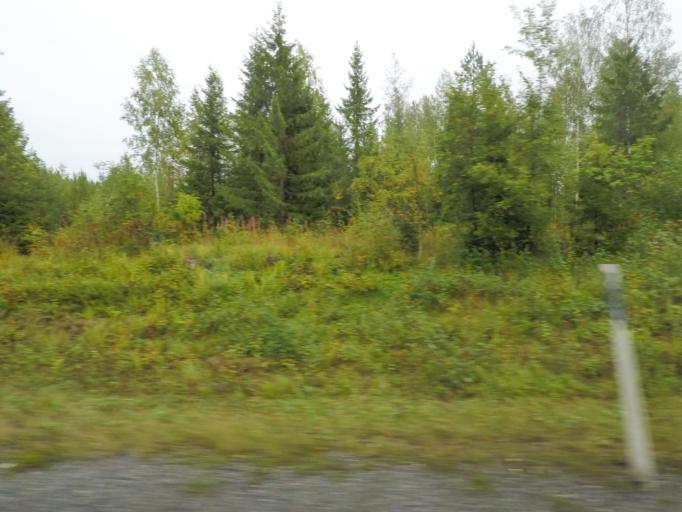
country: FI
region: Southern Savonia
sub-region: Pieksaemaeki
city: Juva
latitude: 62.0172
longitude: 27.7996
